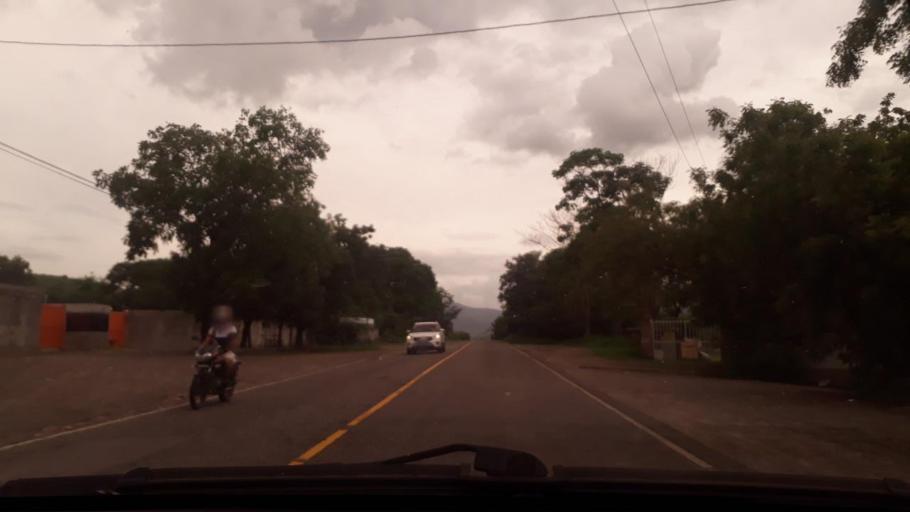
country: GT
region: Chiquimula
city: San Jose La Arada
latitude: 14.7469
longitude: -89.5412
